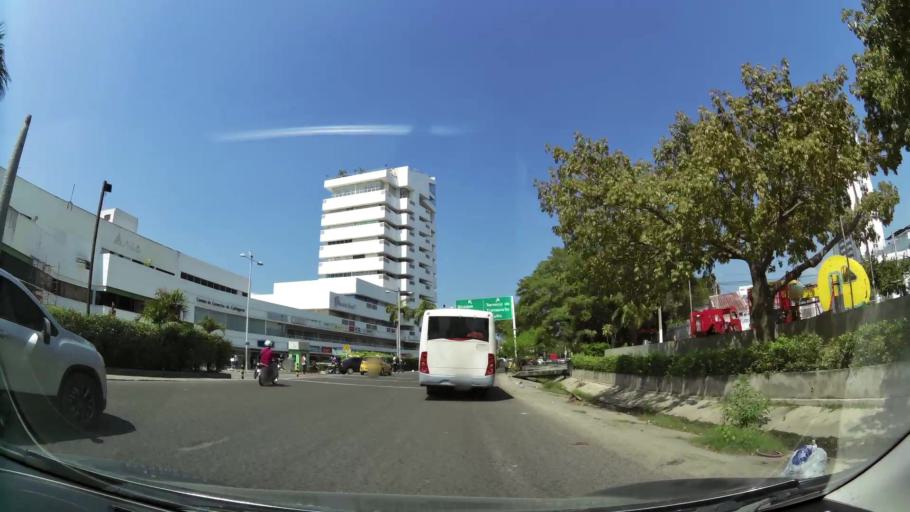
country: CO
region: Bolivar
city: Cartagena
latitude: 10.3927
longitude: -75.4810
